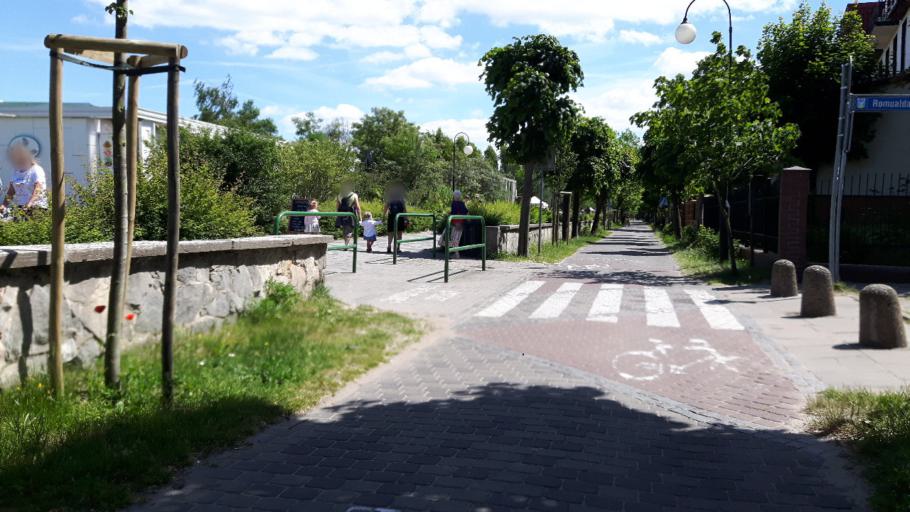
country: PL
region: Pomeranian Voivodeship
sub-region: Sopot
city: Sopot
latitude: 54.4408
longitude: 18.5758
